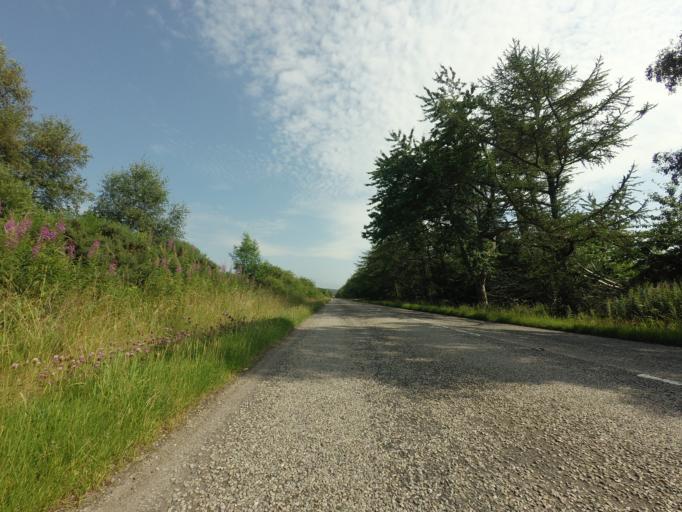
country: GB
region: Scotland
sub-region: Highland
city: Evanton
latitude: 57.9175
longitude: -4.3933
